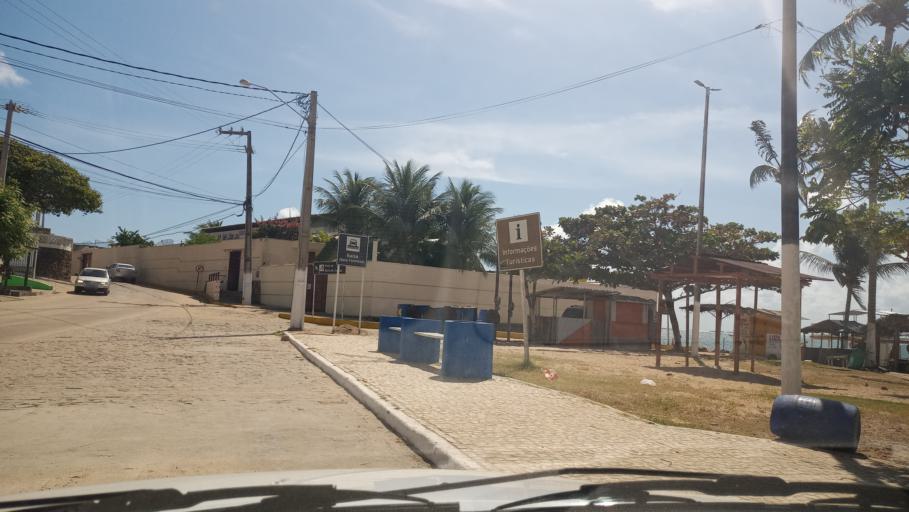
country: BR
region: Rio Grande do Norte
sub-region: Canguaretama
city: Canguaretama
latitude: -6.3125
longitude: -35.0401
